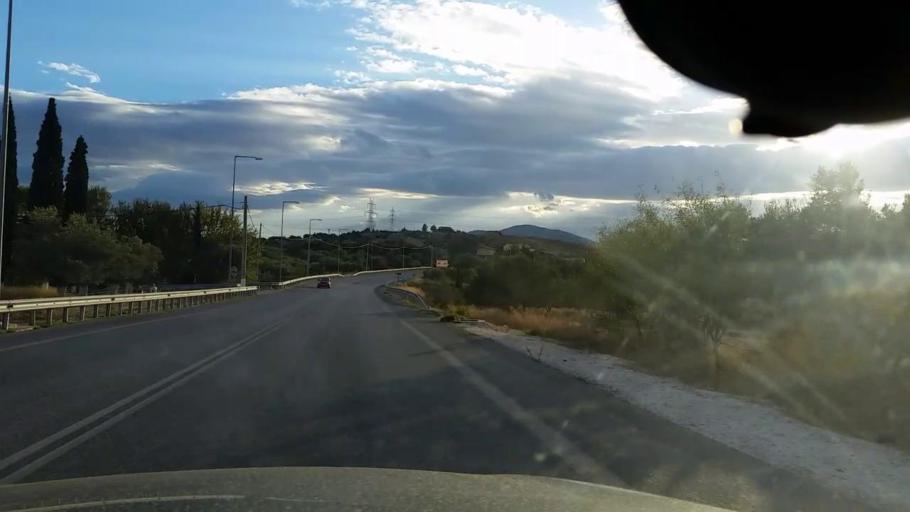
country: GR
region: Attica
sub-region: Nomarchia Anatolikis Attikis
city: Argithea
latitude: 37.9592
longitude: 23.8946
